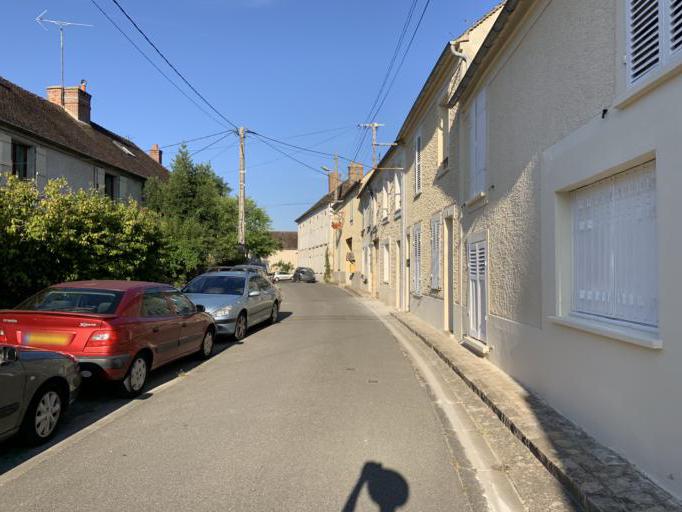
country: FR
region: Ile-de-France
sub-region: Departement de Seine-et-Marne
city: Grez-sur-Loing
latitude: 48.3468
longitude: 2.6434
